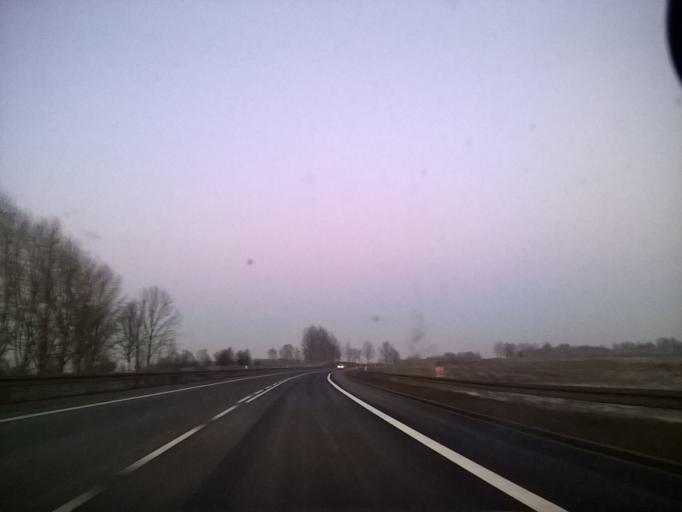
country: PL
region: Warmian-Masurian Voivodeship
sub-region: Powiat olsztynski
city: Czerwonka
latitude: 53.8284
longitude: 20.8729
